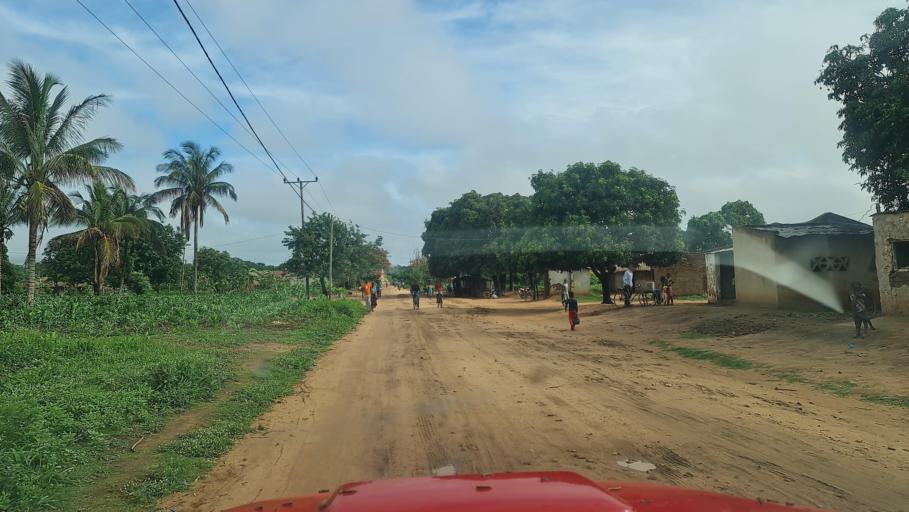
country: MW
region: Southern Region
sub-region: Nsanje District
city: Nsanje
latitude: -17.3182
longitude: 35.5920
